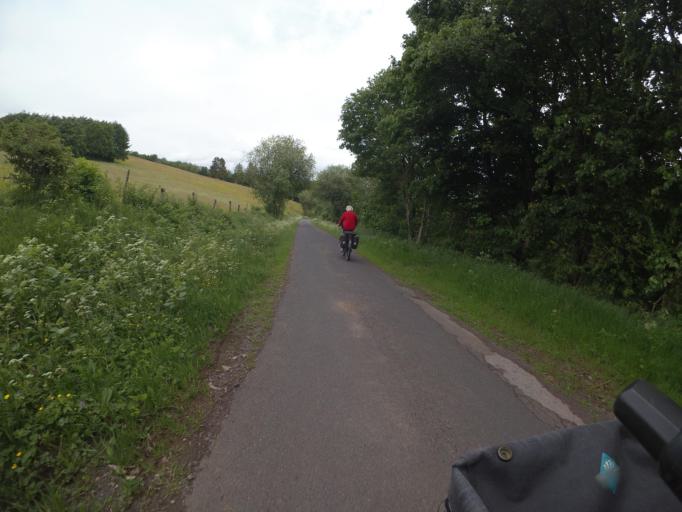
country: DE
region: North Rhine-Westphalia
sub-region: Regierungsbezirk Koln
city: Hellenthal
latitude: 50.4246
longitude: 6.4041
